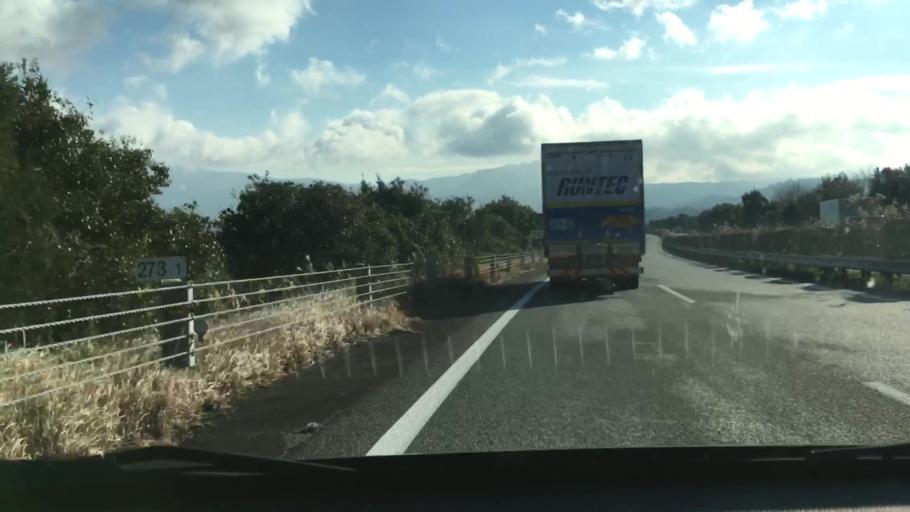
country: JP
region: Kumamoto
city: Hitoyoshi
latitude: 32.0609
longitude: 130.8037
